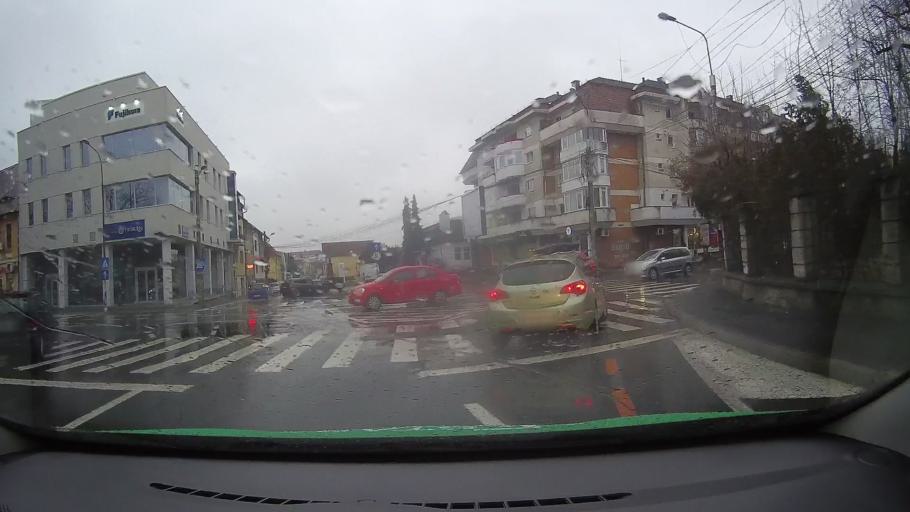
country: RO
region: Sibiu
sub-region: Municipiul Sibiu
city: Sibiu
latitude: 45.7884
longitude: 24.1422
